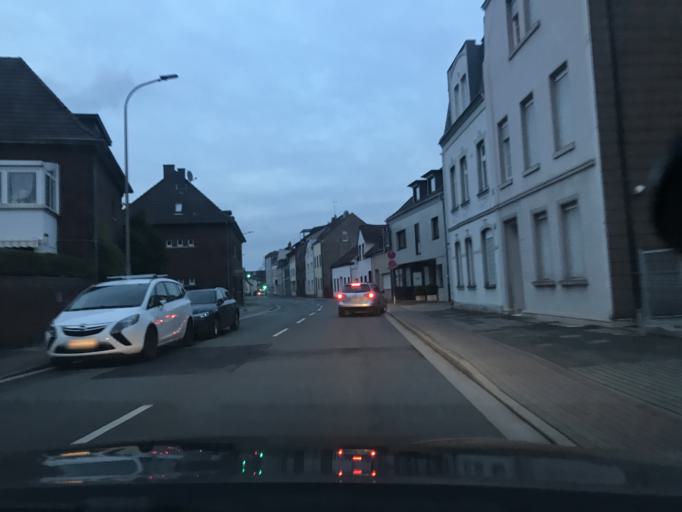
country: DE
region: North Rhine-Westphalia
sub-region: Regierungsbezirk Dusseldorf
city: Moers
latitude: 51.4447
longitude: 6.6266
